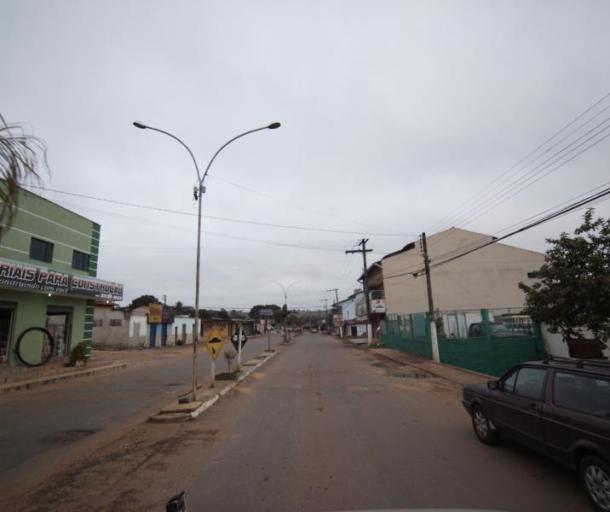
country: BR
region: Goias
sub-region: Pirenopolis
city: Pirenopolis
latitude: -15.9248
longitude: -48.8059
